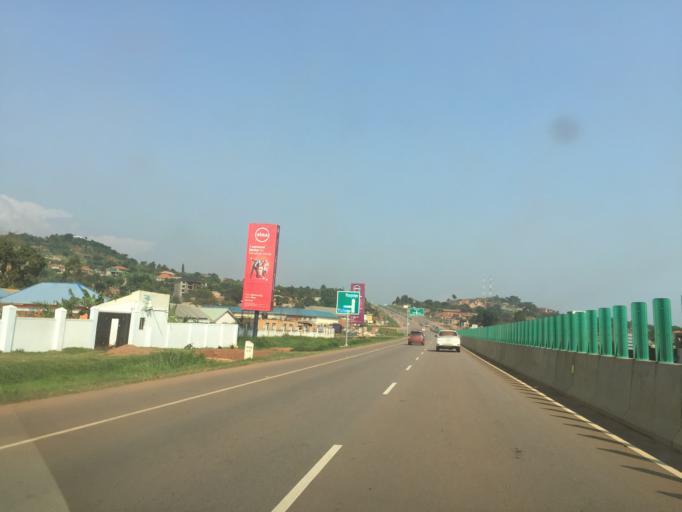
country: UG
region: Central Region
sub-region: Wakiso District
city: Kajansi
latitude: 0.2098
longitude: 32.5669
